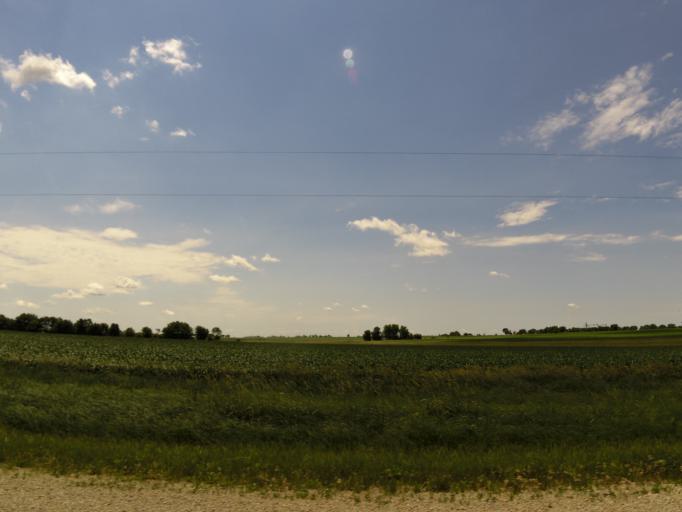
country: US
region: Iowa
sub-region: Buchanan County
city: Fairbank
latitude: 42.7148
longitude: -92.0666
